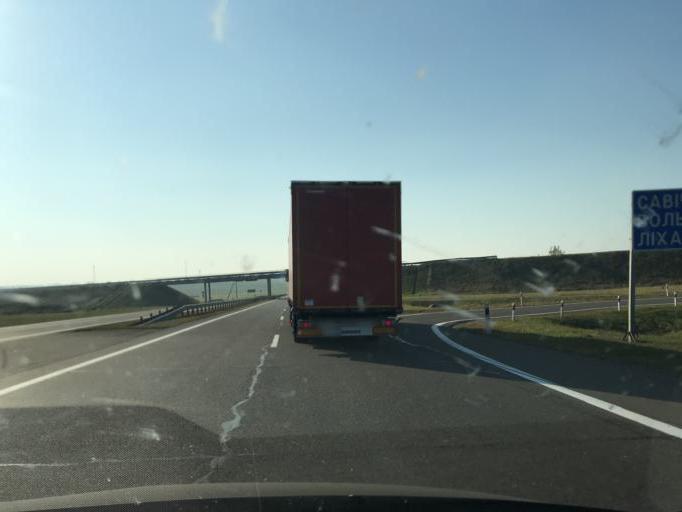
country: BY
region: Minsk
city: Snow
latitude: 53.2682
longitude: 26.2912
